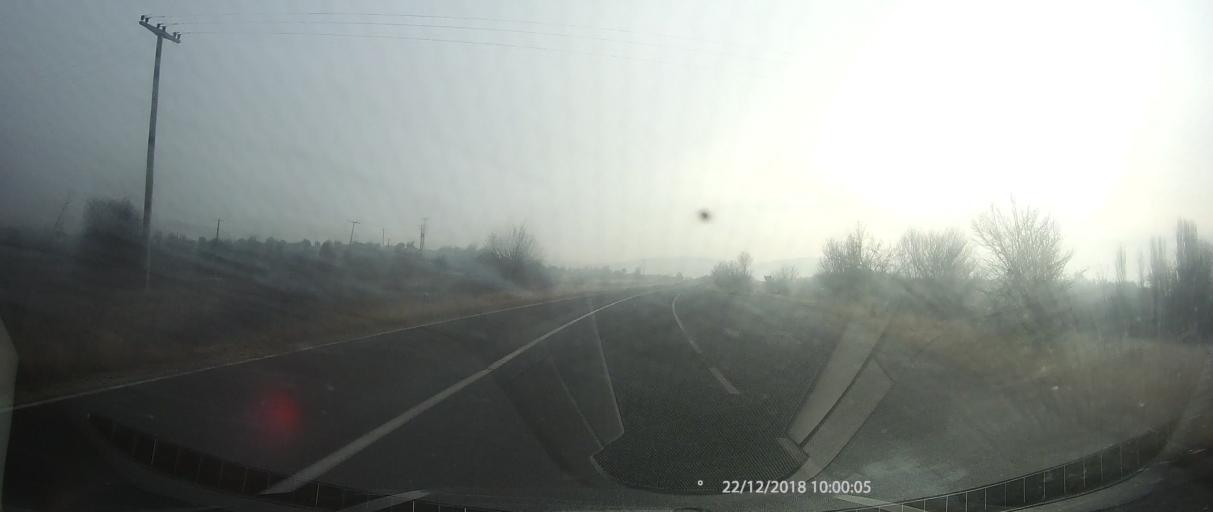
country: MK
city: Klechovce
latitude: 42.1489
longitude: 21.9738
